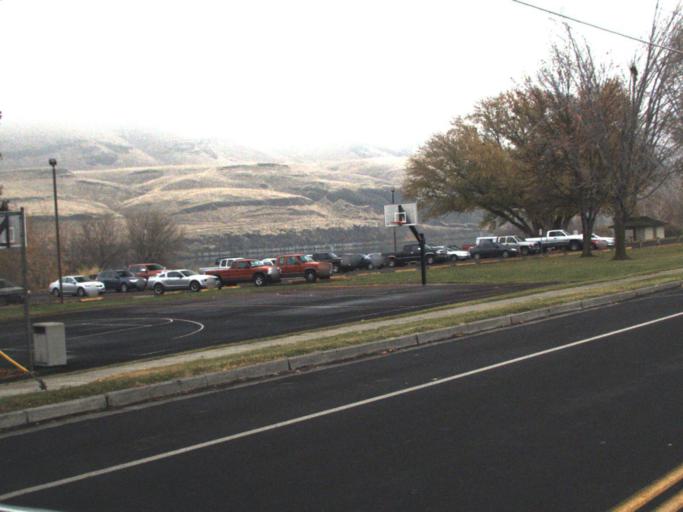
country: US
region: Washington
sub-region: Asotin County
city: Asotin
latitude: 46.3410
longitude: -117.0526
